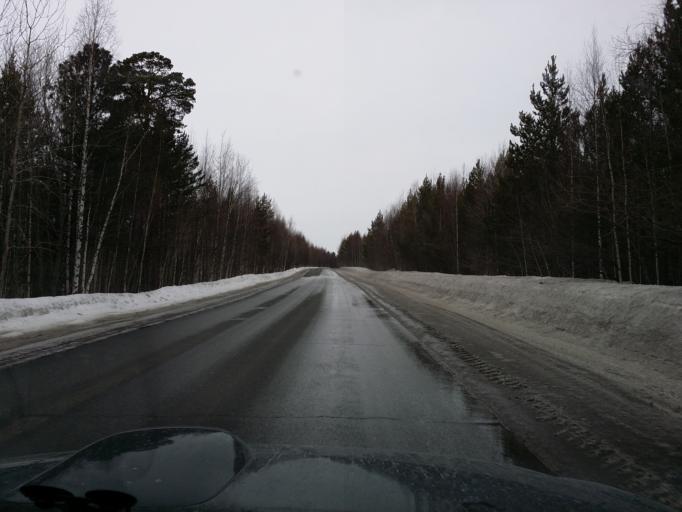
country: RU
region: Tomsk
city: Strezhevoy
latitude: 60.7958
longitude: 77.3098
